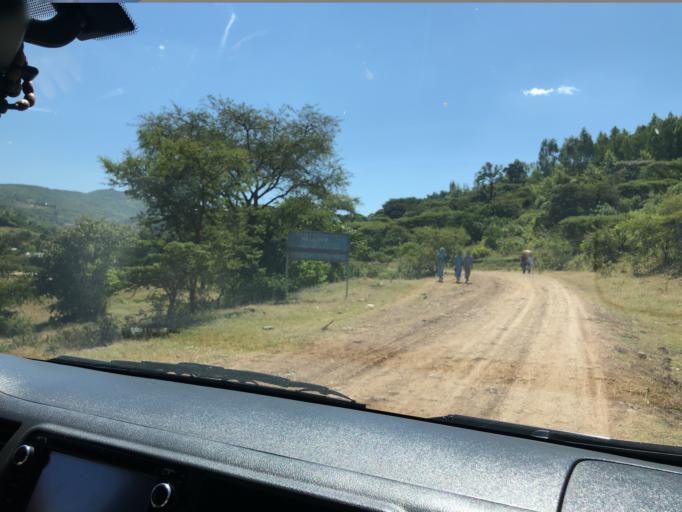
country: ET
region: Amhara
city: Werota
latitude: 11.9231
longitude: 37.7864
